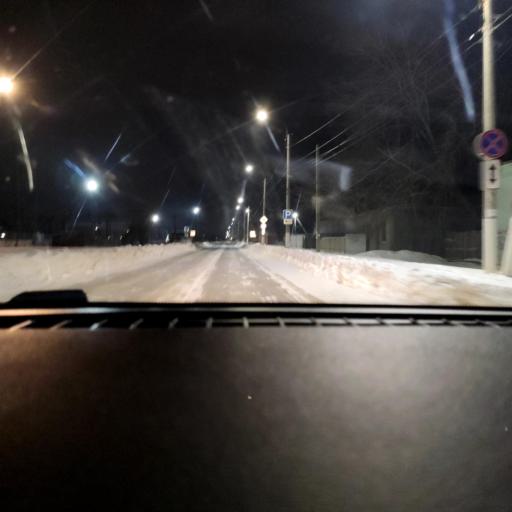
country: RU
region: Samara
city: Chapayevsk
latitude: 52.9793
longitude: 49.7033
